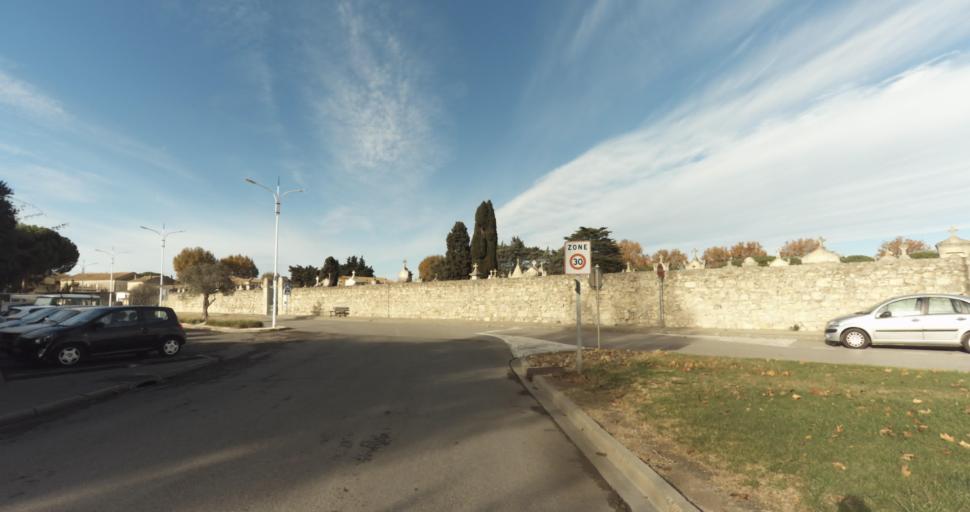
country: FR
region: Languedoc-Roussillon
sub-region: Departement du Gard
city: Aigues-Mortes
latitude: 43.5704
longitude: 4.1947
